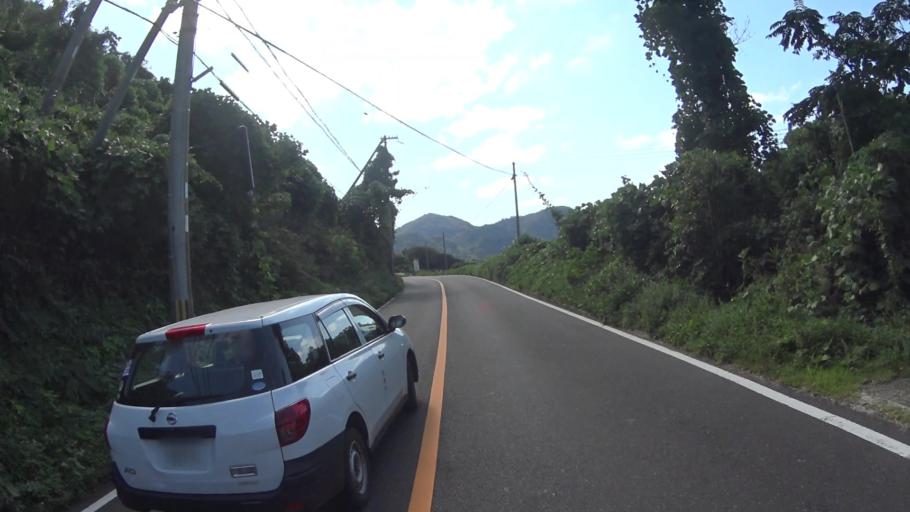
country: JP
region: Kyoto
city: Miyazu
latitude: 35.7522
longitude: 135.1564
